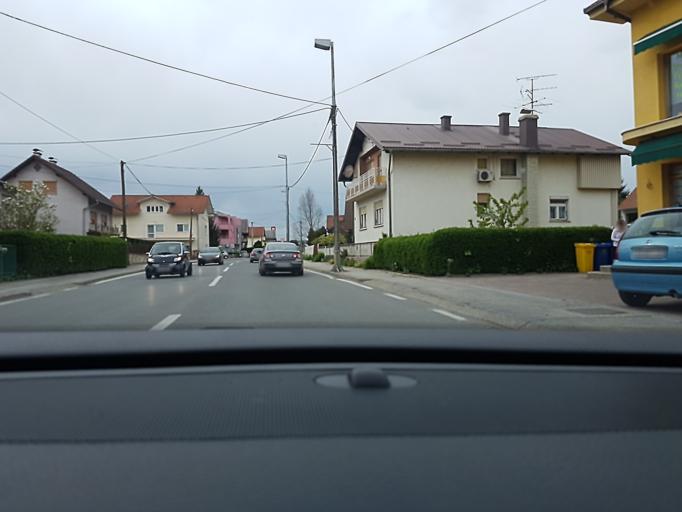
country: HR
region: Zagrebacka
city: Zapresic
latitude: 45.8582
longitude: 15.8021
